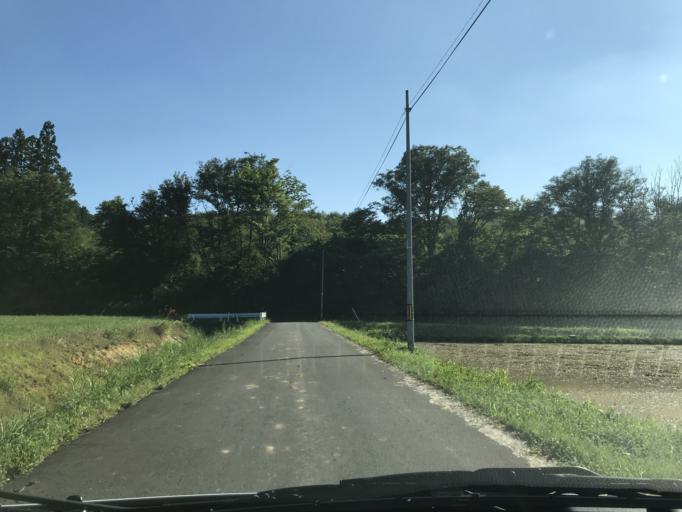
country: JP
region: Iwate
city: Mizusawa
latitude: 39.0732
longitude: 141.0387
